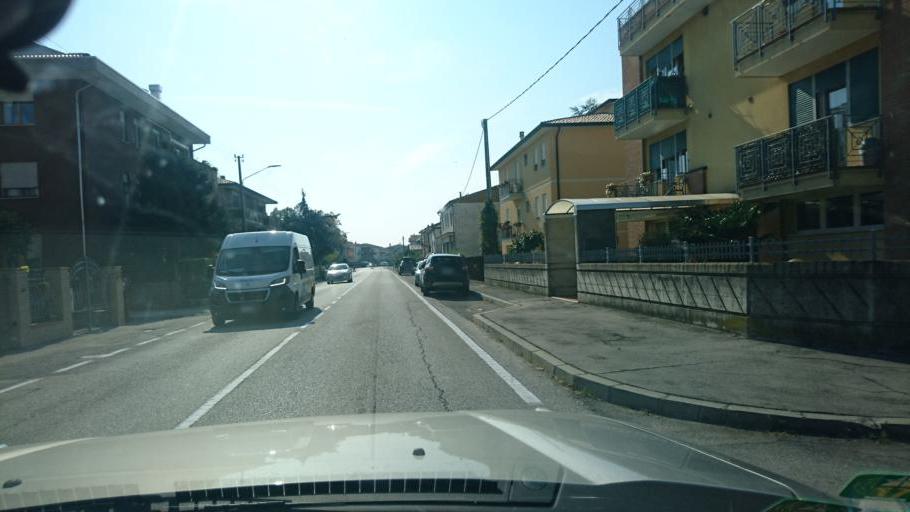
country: IT
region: Veneto
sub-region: Provincia di Padova
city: Caselle
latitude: 45.4024
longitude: 11.8269
